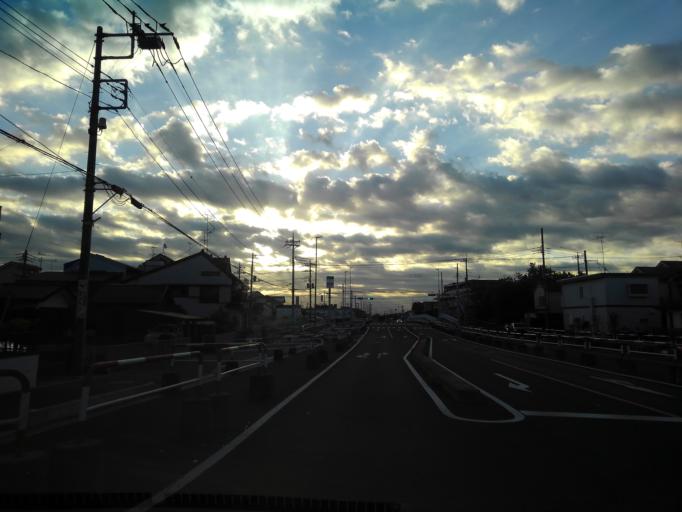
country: JP
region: Saitama
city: Tokorozawa
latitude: 35.7822
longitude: 139.4559
